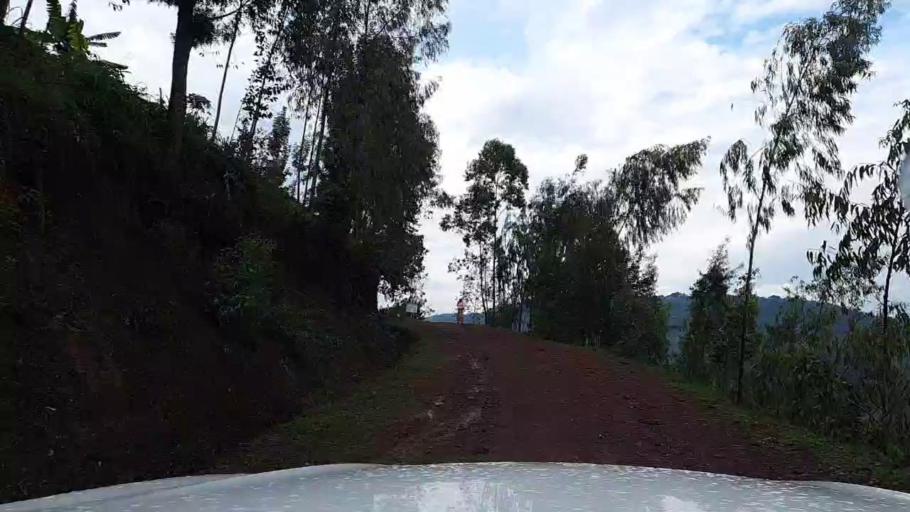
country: RW
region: Northern Province
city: Byumba
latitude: -1.7210
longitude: 29.9171
